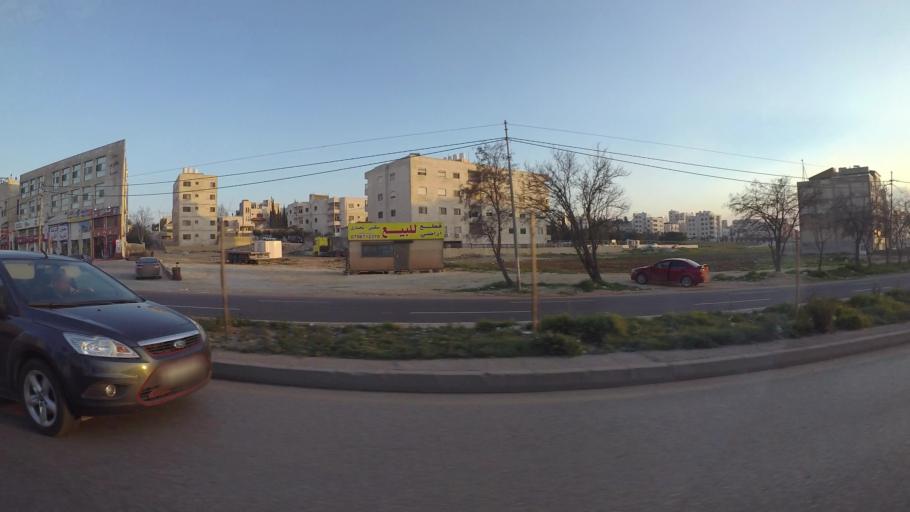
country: JO
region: Amman
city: Al Quwaysimah
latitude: 31.9004
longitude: 35.9266
